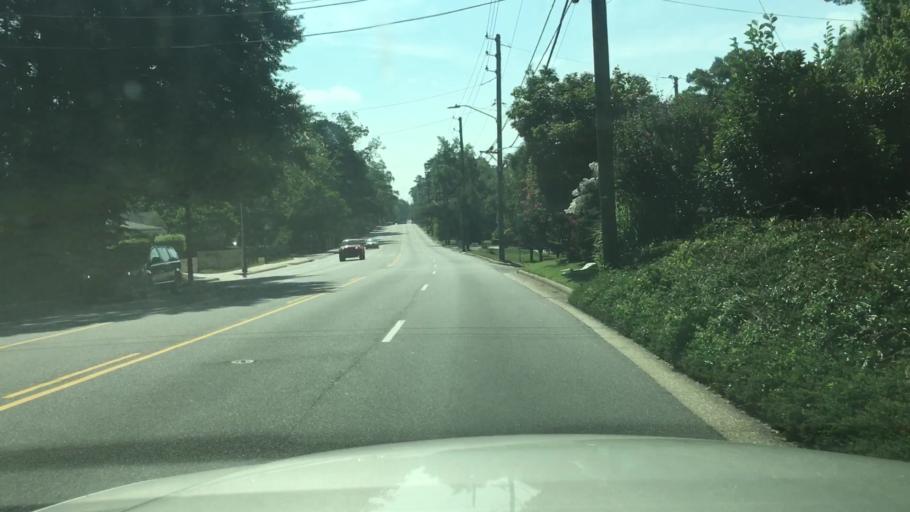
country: US
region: North Carolina
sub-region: Cumberland County
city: Fayetteville
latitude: 35.0605
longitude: -78.9152
